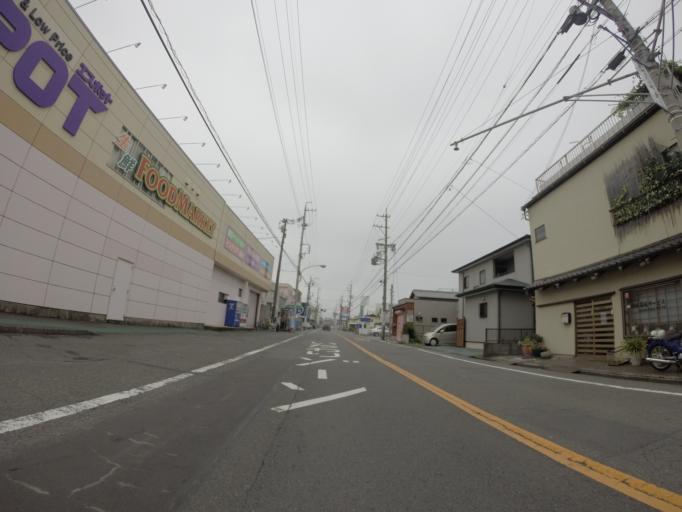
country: JP
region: Shizuoka
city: Shizuoka-shi
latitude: 34.9543
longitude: 138.3933
